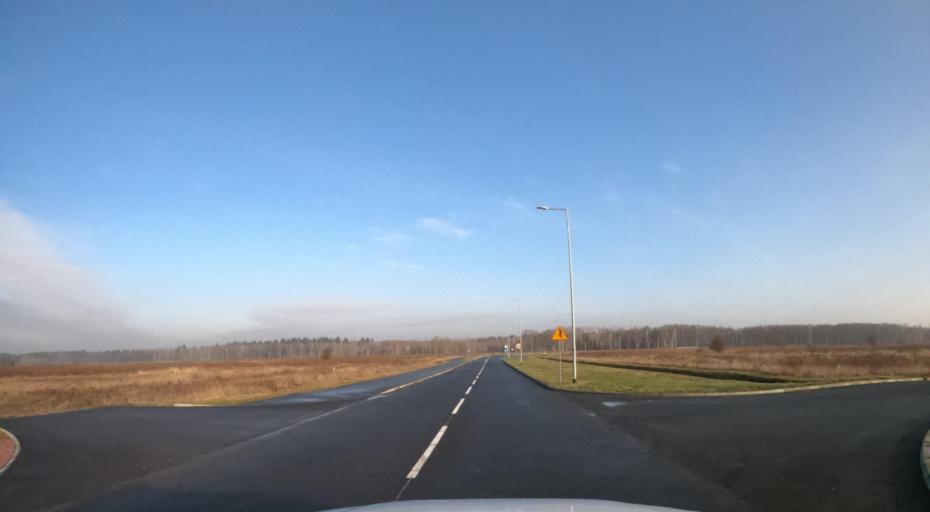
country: PL
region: Lubusz
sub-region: Powiat gorzowski
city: Kostrzyn nad Odra
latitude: 52.6278
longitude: 14.6128
